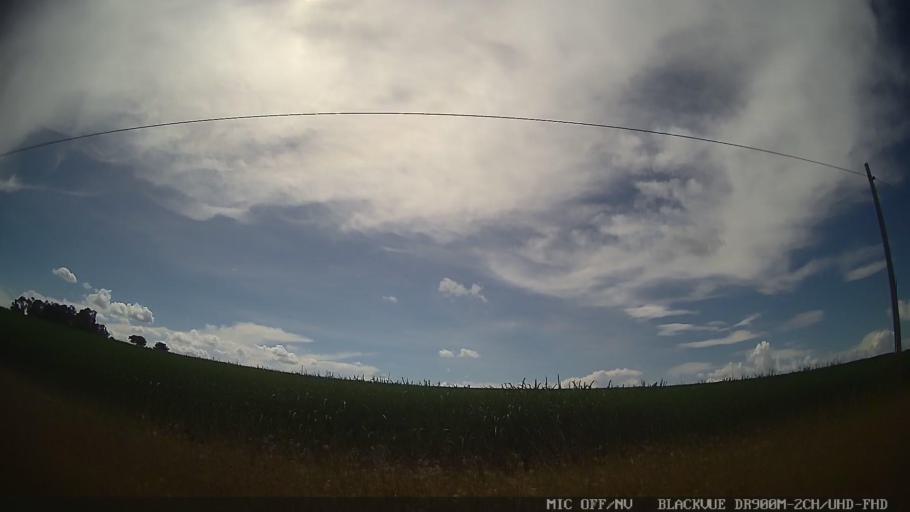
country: BR
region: Sao Paulo
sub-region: Conchas
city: Conchas
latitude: -22.9763
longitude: -47.9879
